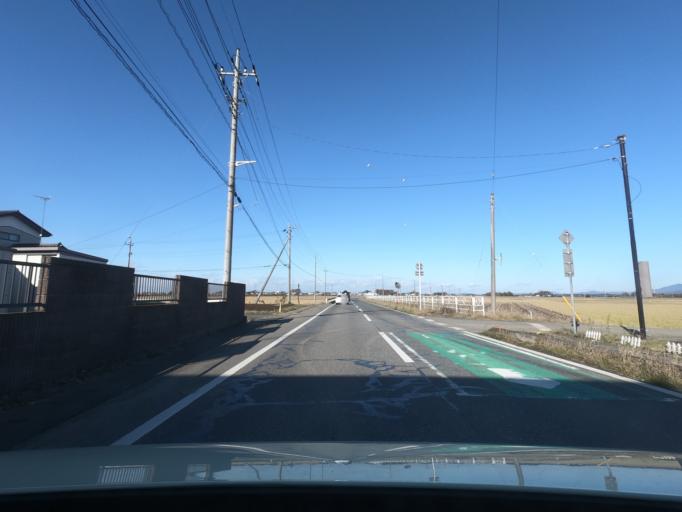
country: JP
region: Ibaraki
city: Ishige
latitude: 36.1523
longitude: 139.9965
